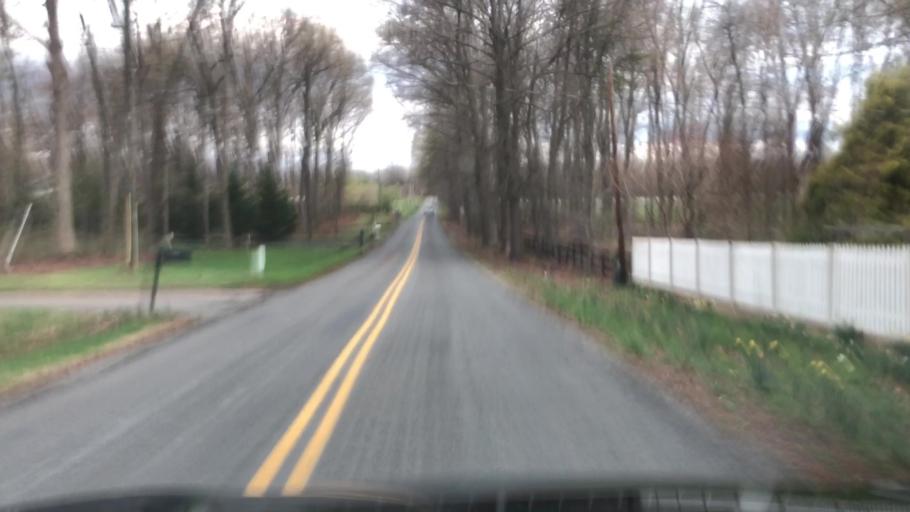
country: US
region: Virginia
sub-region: Fauquier County
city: New Baltimore
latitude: 38.7335
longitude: -77.6707
